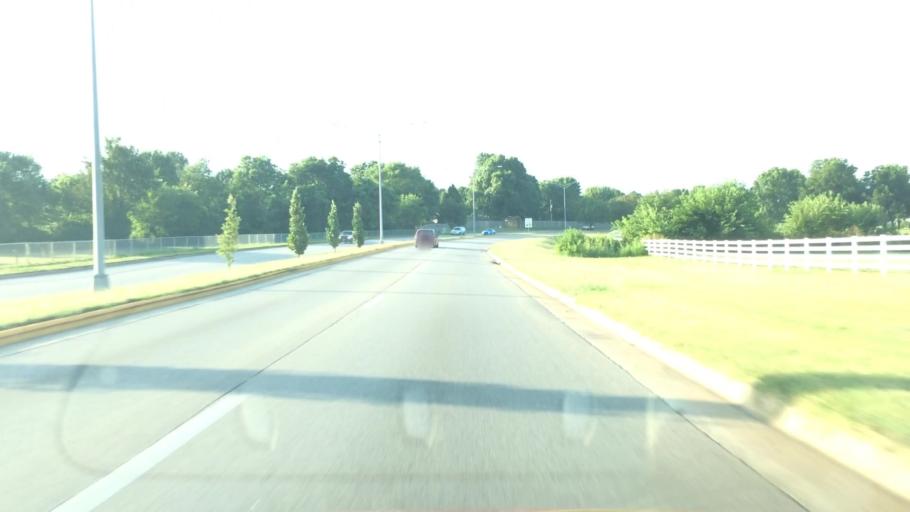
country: US
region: Missouri
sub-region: Greene County
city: Springfield
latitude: 37.1746
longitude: -93.3171
